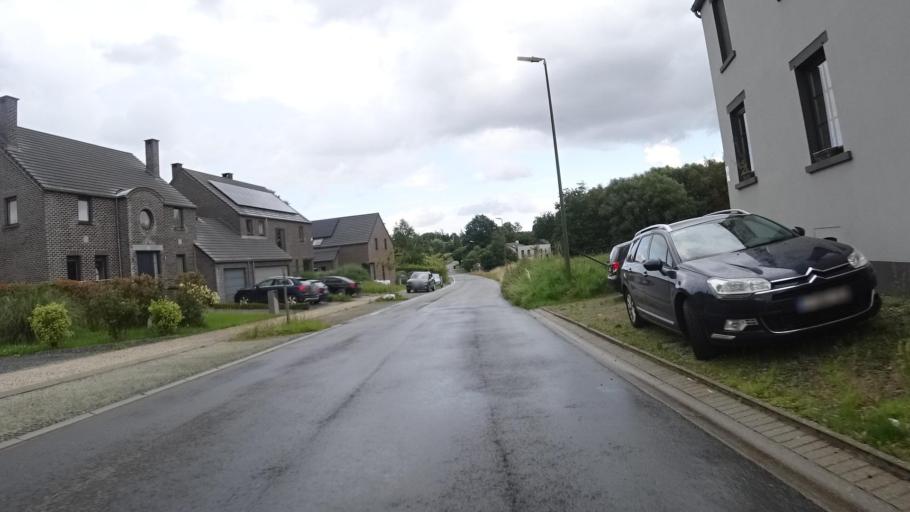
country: BE
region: Wallonia
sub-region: Province de Namur
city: Sombreffe
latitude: 50.5708
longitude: 4.6010
